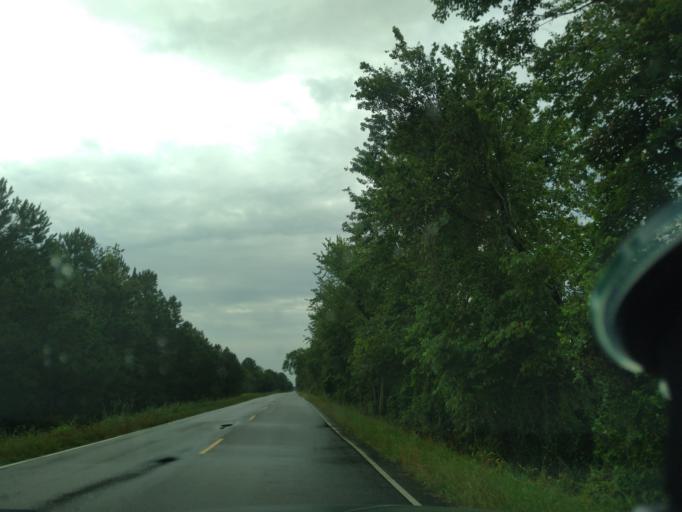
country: US
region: North Carolina
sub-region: Washington County
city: Plymouth
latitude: 35.8421
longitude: -76.5486
